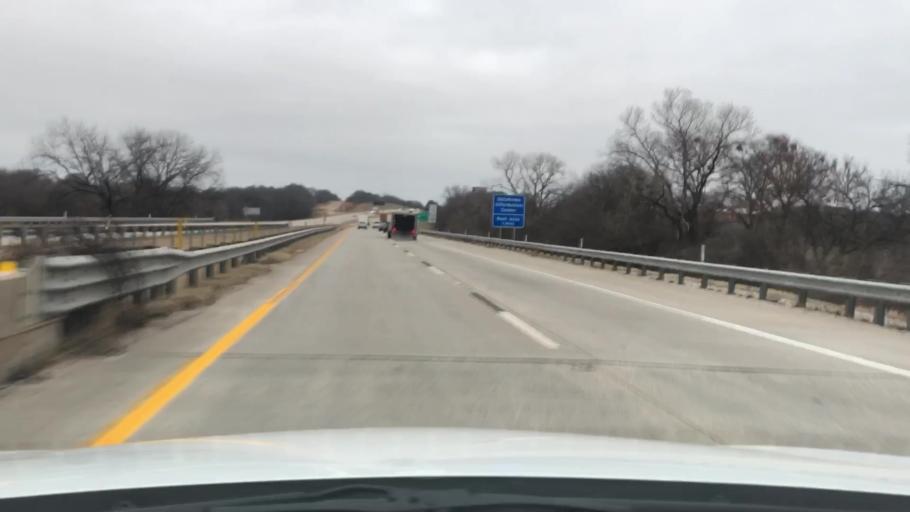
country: US
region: Texas
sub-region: Cooke County
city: Gainesville
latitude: 33.7292
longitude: -97.1575
